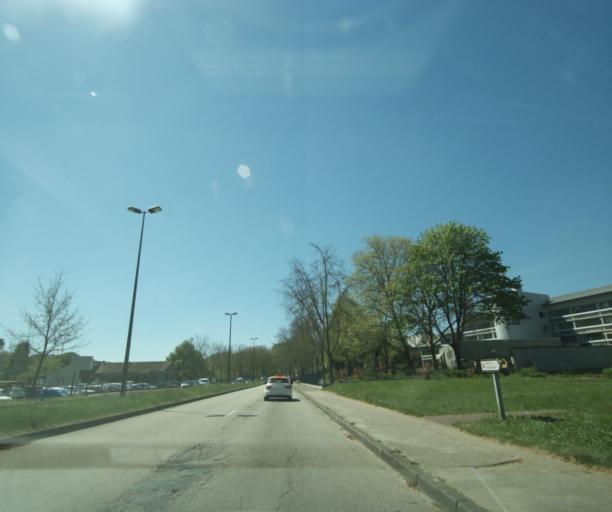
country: FR
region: Limousin
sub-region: Departement de la Haute-Vienne
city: Limoges
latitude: 45.8318
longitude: 1.2732
